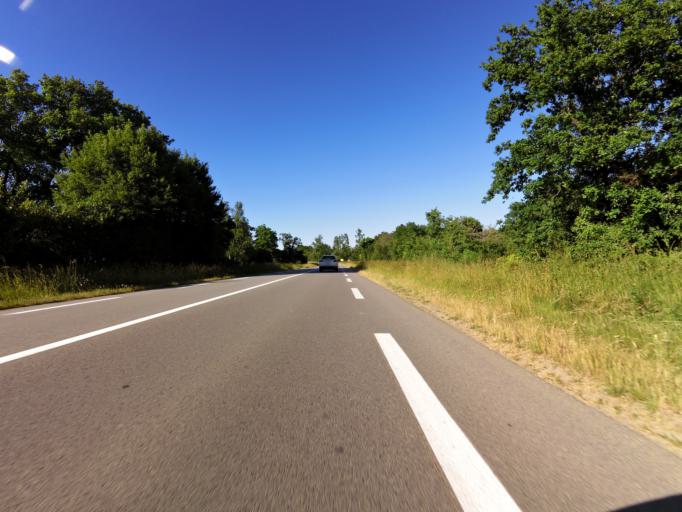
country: FR
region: Brittany
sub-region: Departement du Morbihan
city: Ferel
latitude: 47.5123
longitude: -2.3744
